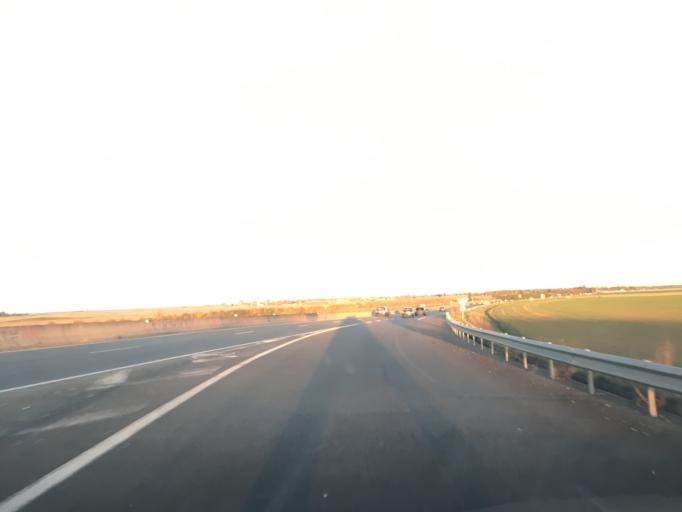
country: FR
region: Haute-Normandie
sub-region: Departement de l'Eure
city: Gravigny
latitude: 49.0142
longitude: 1.1987
